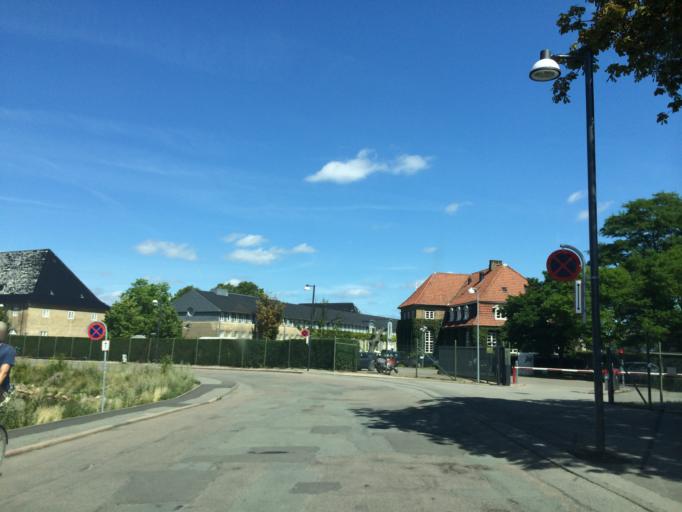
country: DK
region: Capital Region
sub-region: Kobenhavn
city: Christianshavn
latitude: 55.6769
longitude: 12.6012
